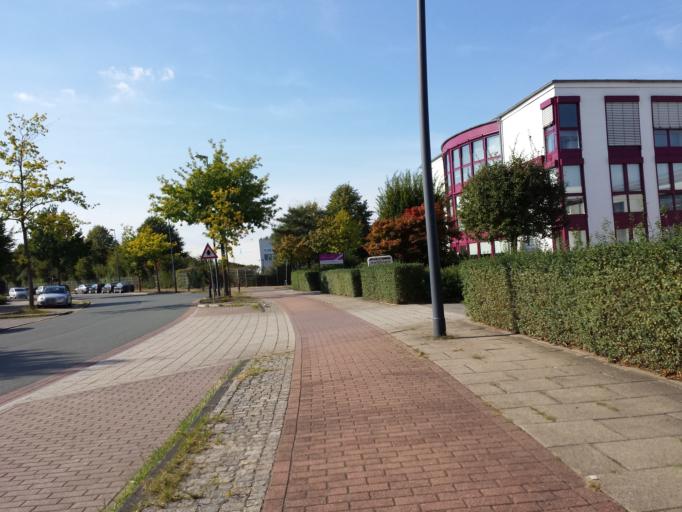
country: DE
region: Bremen
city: Bremen
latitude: 53.0483
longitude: 8.8359
